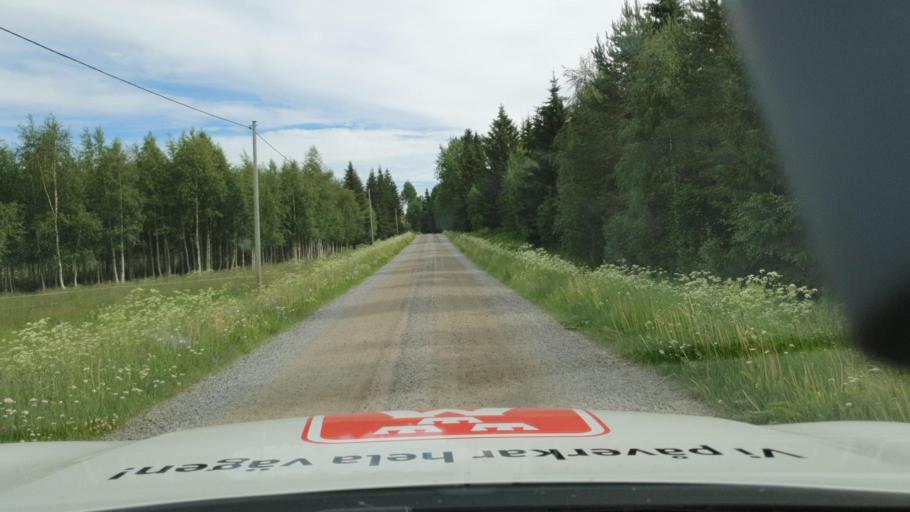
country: SE
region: Vaesterbotten
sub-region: Robertsfors Kommun
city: Robertsfors
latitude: 64.3938
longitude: 21.0204
